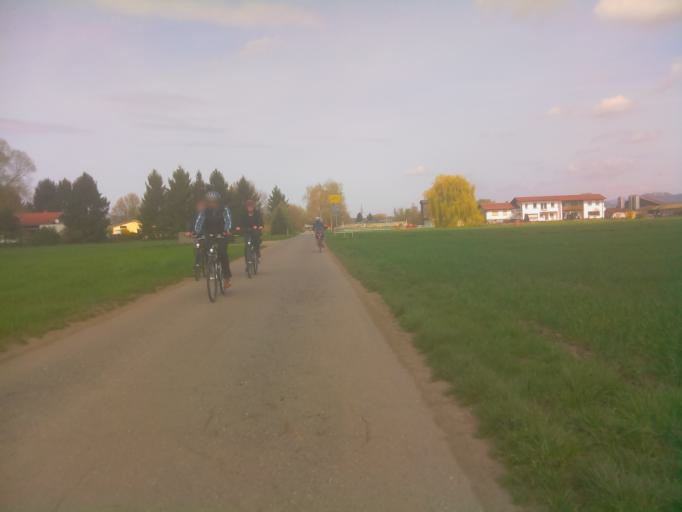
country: DE
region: Baden-Wuerttemberg
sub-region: Karlsruhe Region
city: Hemsbach
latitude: 49.5912
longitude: 8.6181
